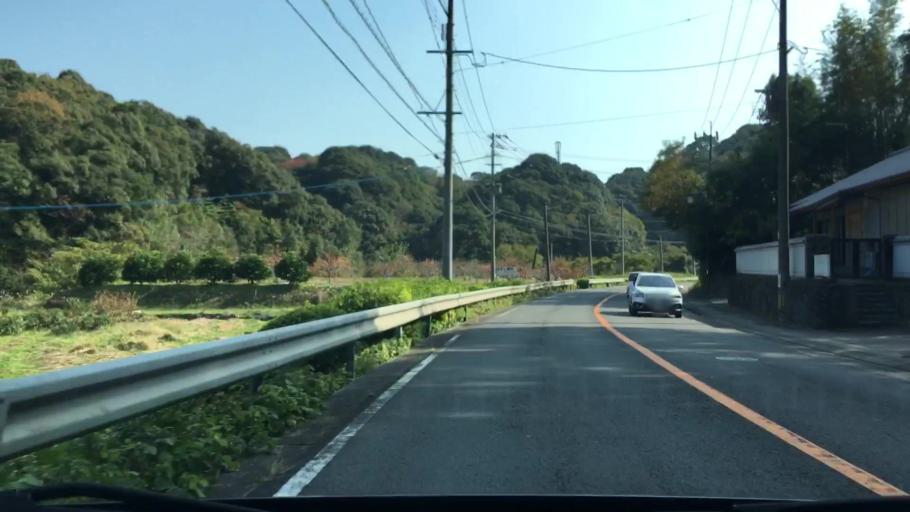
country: JP
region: Nagasaki
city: Togitsu
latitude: 32.9558
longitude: 129.7844
